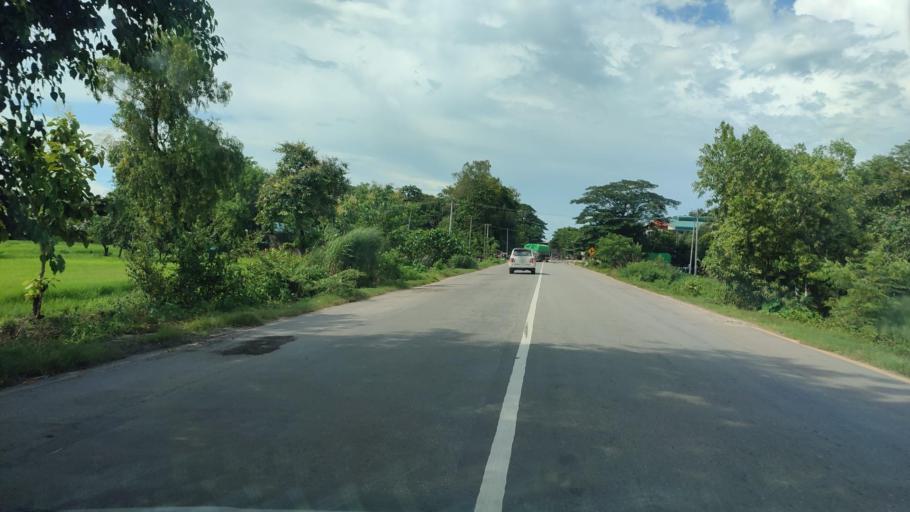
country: MM
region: Bago
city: Nyaunglebin
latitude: 18.2065
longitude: 96.5628
